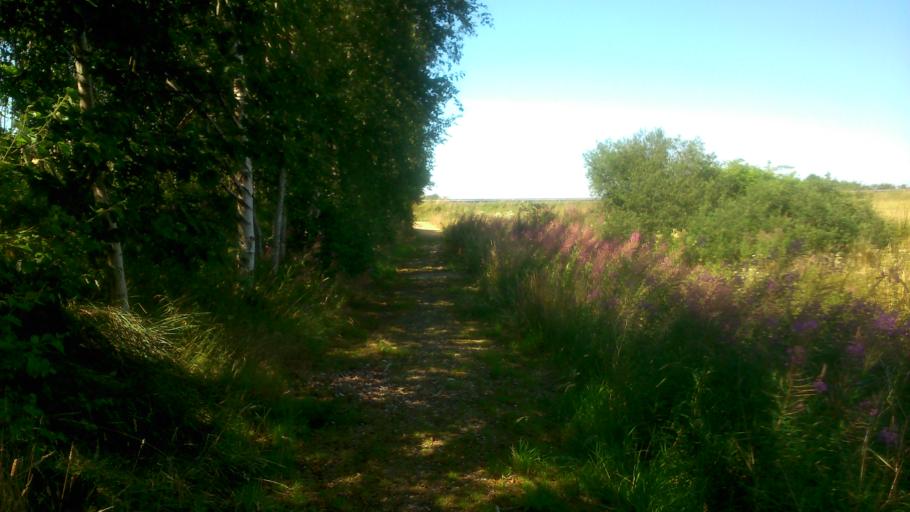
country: DK
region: Central Jutland
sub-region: Ringkobing-Skjern Kommune
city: Skjern
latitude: 56.0199
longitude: 8.5216
